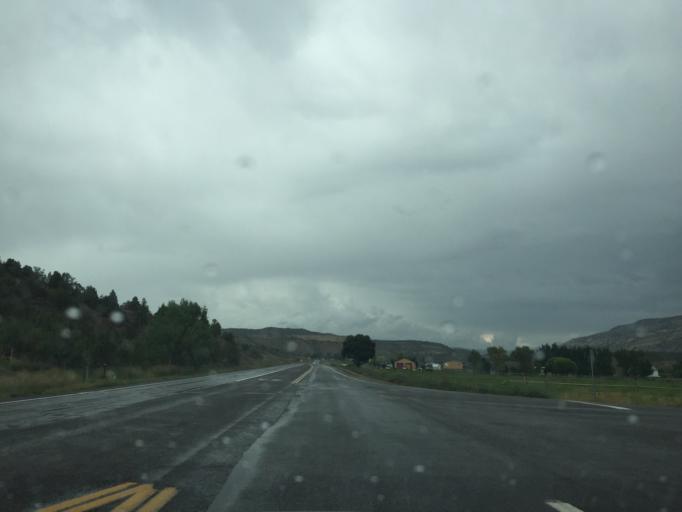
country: US
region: Utah
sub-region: Kane County
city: Kanab
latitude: 37.2590
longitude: -112.6576
